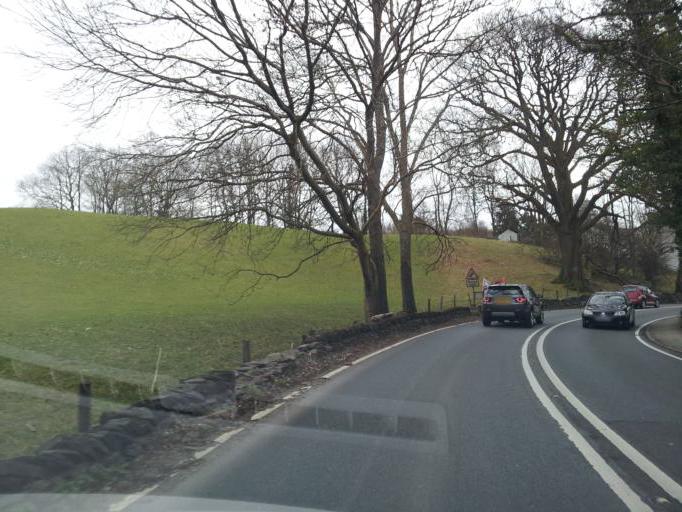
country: GB
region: England
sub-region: Cumbria
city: Ambleside
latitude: 54.4118
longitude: -2.9491
